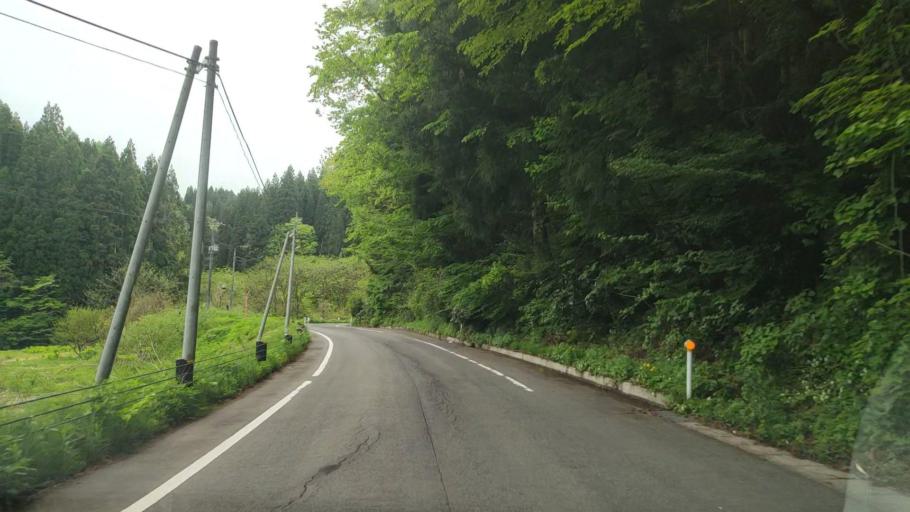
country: JP
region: Niigata
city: Gosen
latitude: 37.7149
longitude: 139.1235
